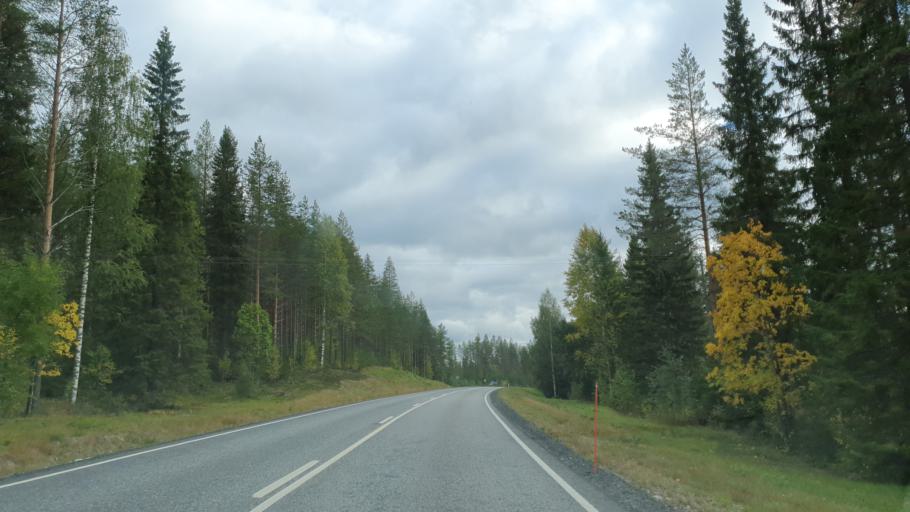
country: FI
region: Kainuu
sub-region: Kehys-Kainuu
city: Kuhmo
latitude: 63.9901
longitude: 29.6410
